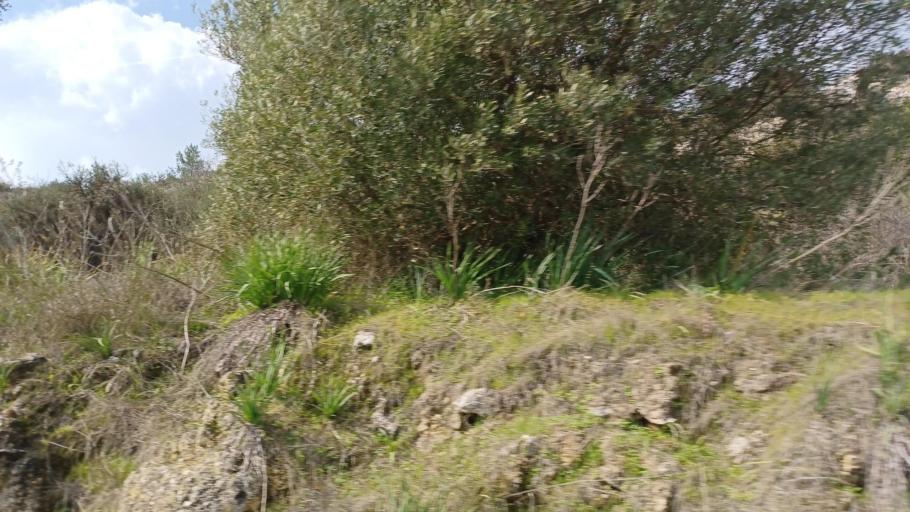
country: CY
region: Pafos
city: Polis
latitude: 35.0201
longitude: 32.4842
